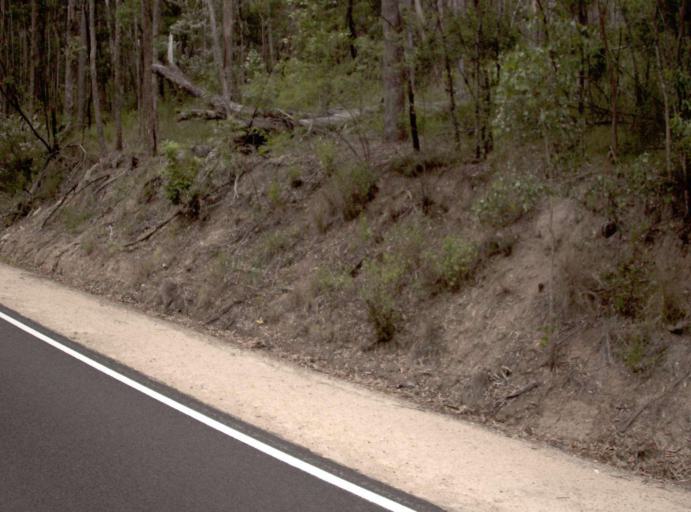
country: AU
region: New South Wales
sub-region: Bombala
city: Bombala
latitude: -37.4649
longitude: 149.1850
